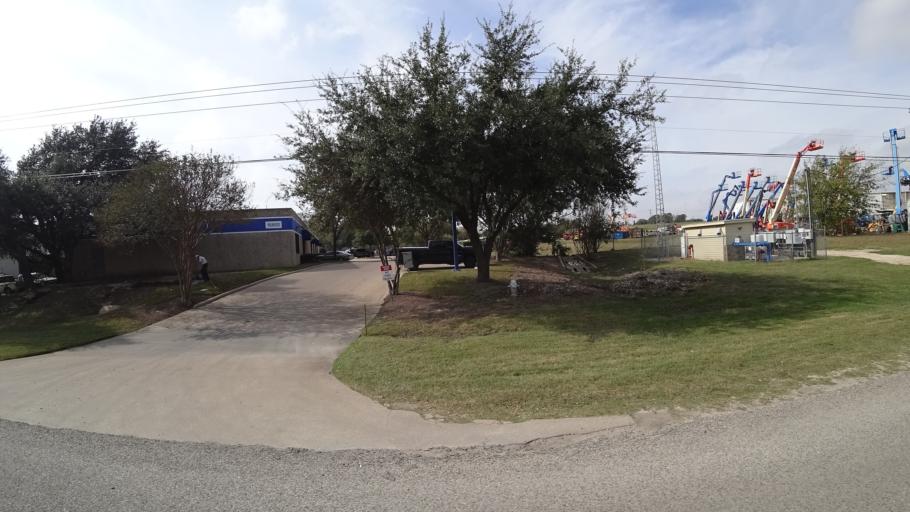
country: US
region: Texas
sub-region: Travis County
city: Windemere
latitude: 30.4536
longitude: -97.6634
